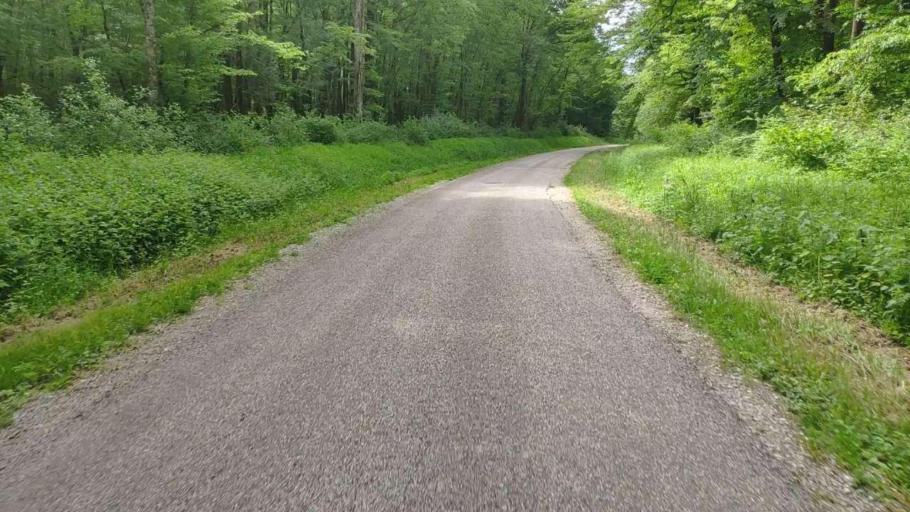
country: FR
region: Franche-Comte
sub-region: Departement du Jura
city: Bletterans
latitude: 46.6934
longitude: 5.4235
